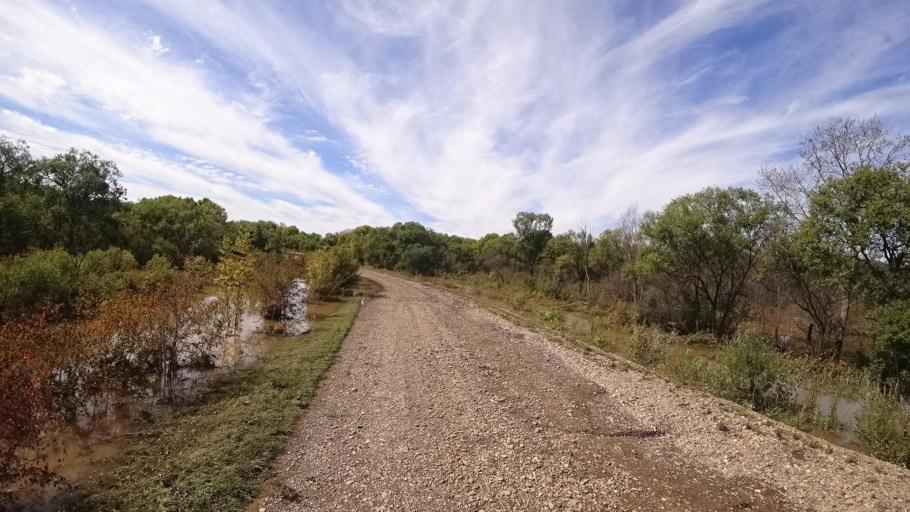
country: RU
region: Primorskiy
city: Kirovskiy
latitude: 44.7641
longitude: 133.6130
